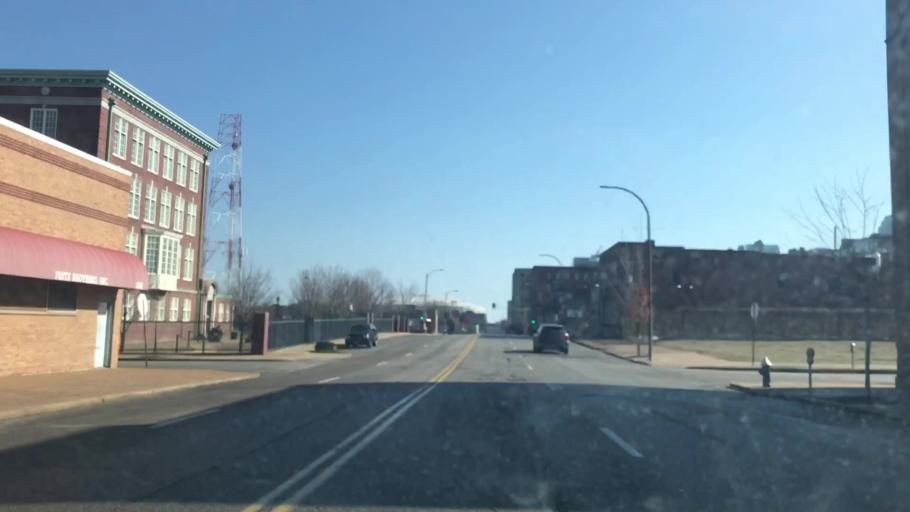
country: US
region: Missouri
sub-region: City of Saint Louis
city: St. Louis
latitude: 38.6353
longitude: -90.2061
